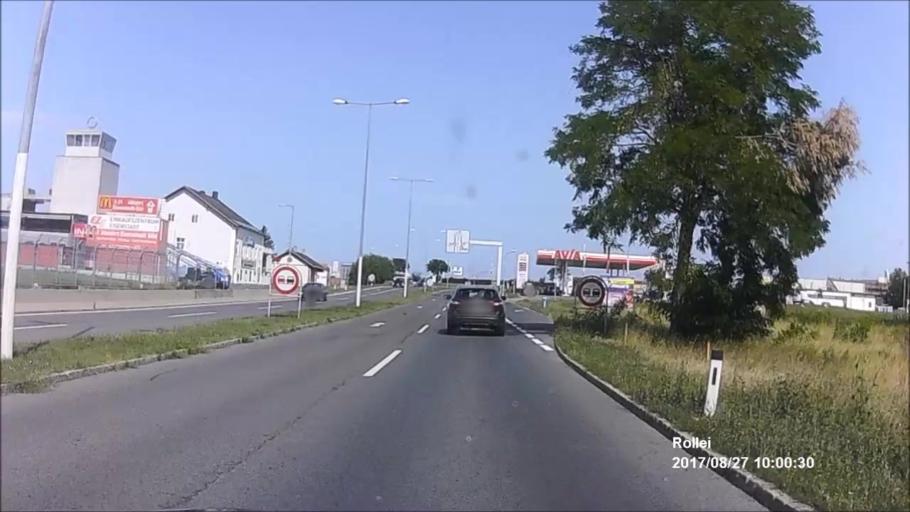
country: AT
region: Burgenland
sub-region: Eisenstadt-Umgebung
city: Zagersdorf
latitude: 47.7721
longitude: 16.5295
